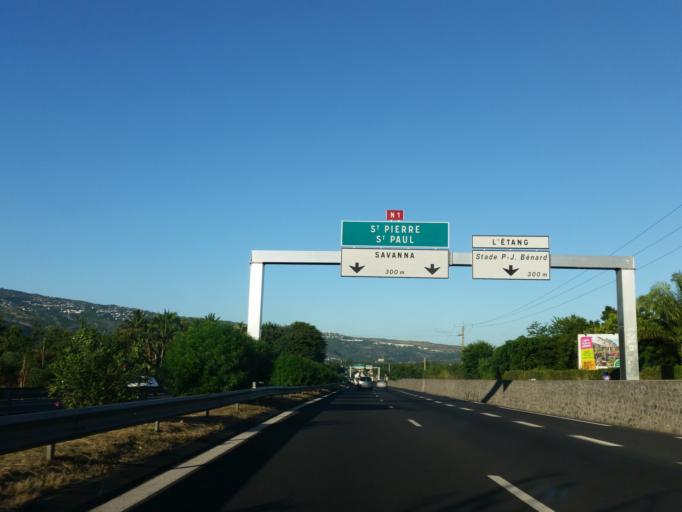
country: RE
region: Reunion
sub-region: Reunion
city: Le Port
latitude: -20.9758
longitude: 55.2973
